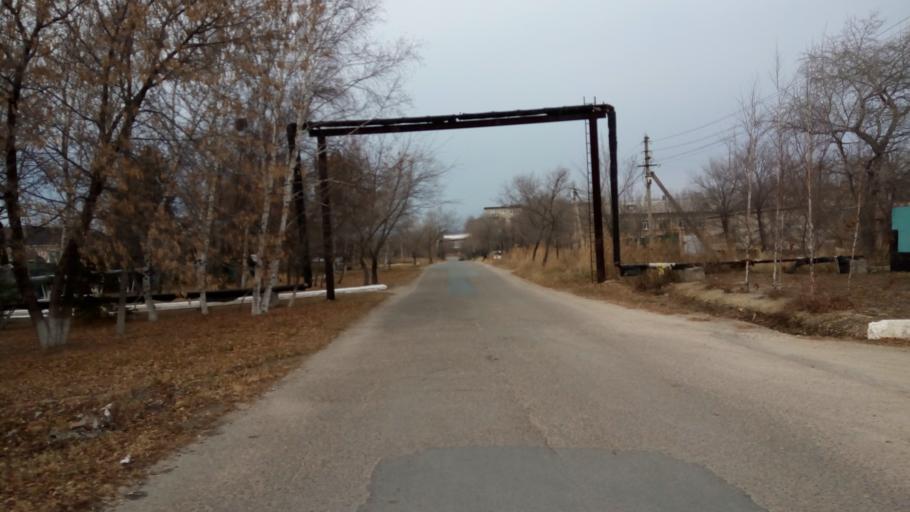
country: RU
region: Primorskiy
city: Novoshakhtinskiy
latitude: 44.0236
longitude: 132.1622
